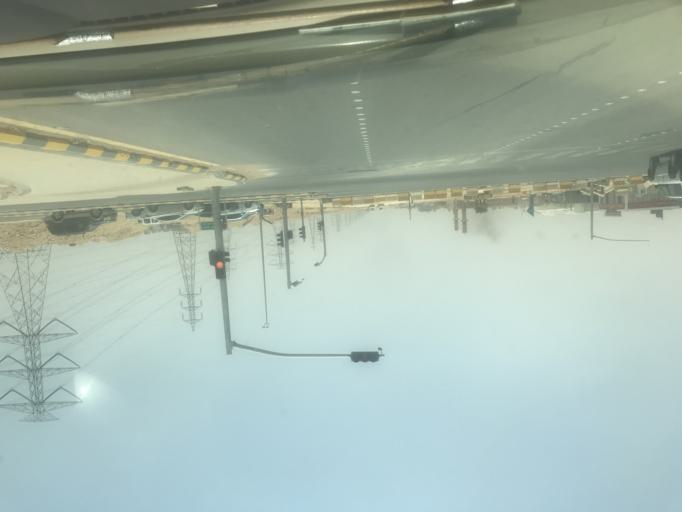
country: SA
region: Ar Riyad
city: Riyadh
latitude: 24.8237
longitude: 46.7493
